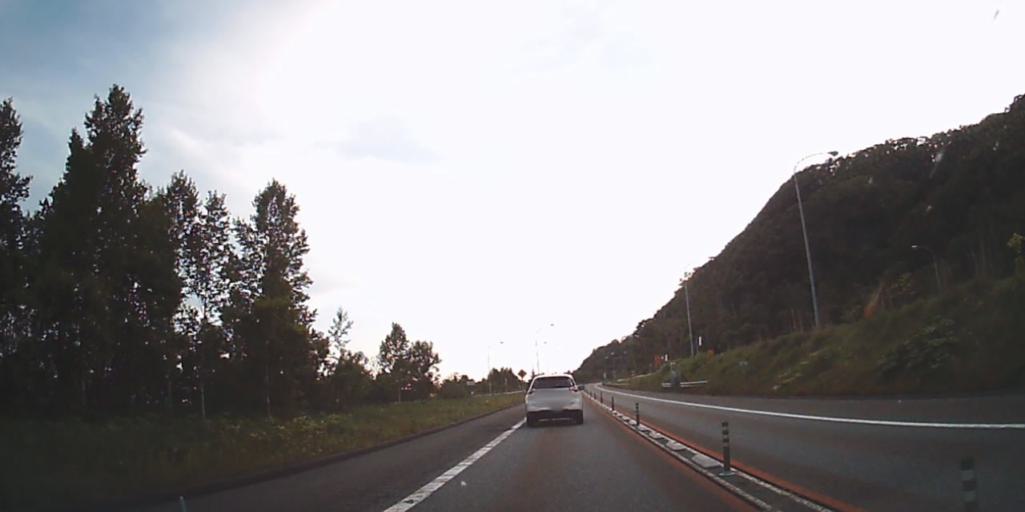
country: JP
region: Hokkaido
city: Niseko Town
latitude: 42.5921
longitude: 140.6960
